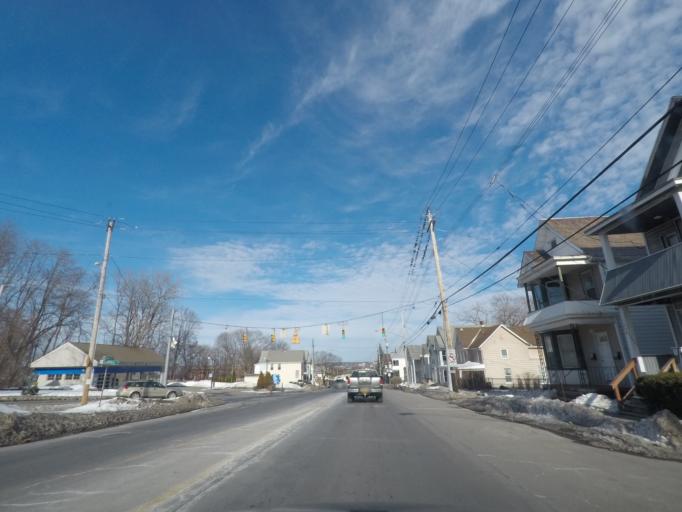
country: US
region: New York
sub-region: Schenectady County
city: Rotterdam
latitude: 42.8008
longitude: -73.9590
